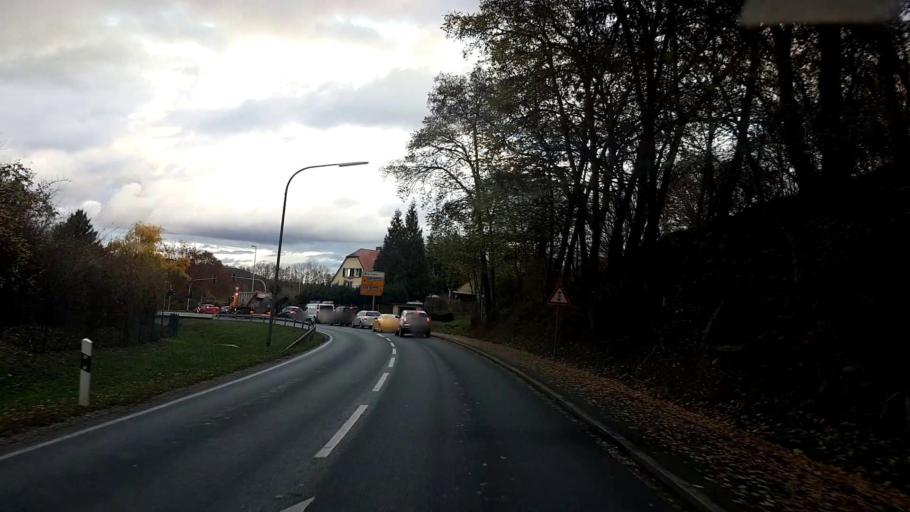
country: DE
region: Bavaria
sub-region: Upper Franconia
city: Oberhaid
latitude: 49.9149
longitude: 10.8137
